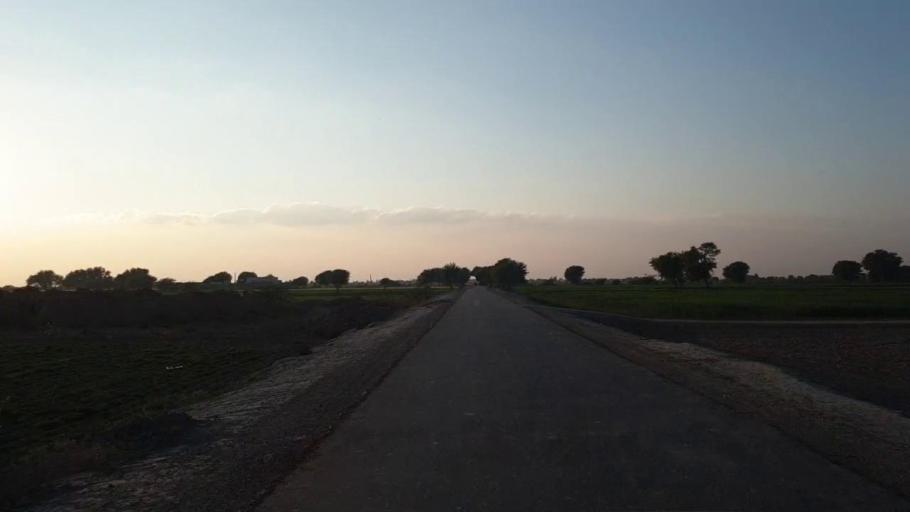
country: PK
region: Sindh
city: Shahpur Chakar
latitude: 26.1560
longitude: 68.5564
